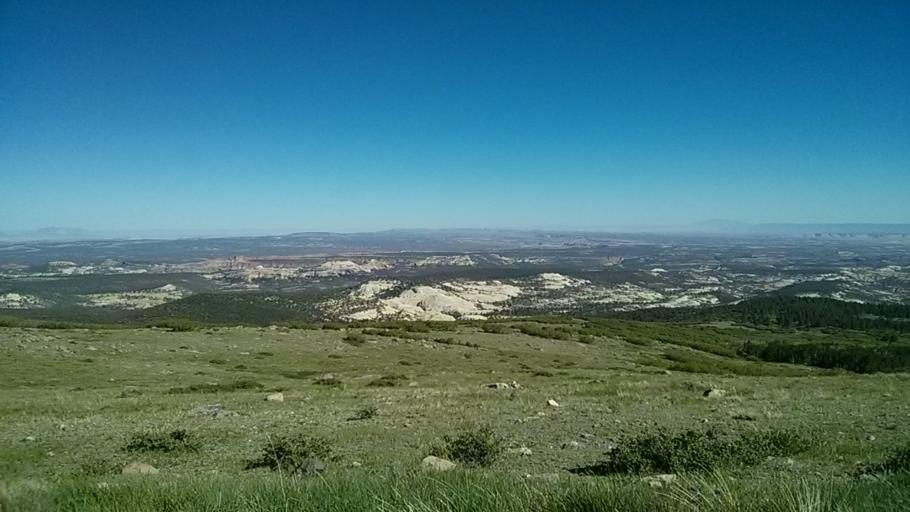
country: US
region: Utah
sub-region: Wayne County
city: Loa
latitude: 38.0117
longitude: -111.3586
